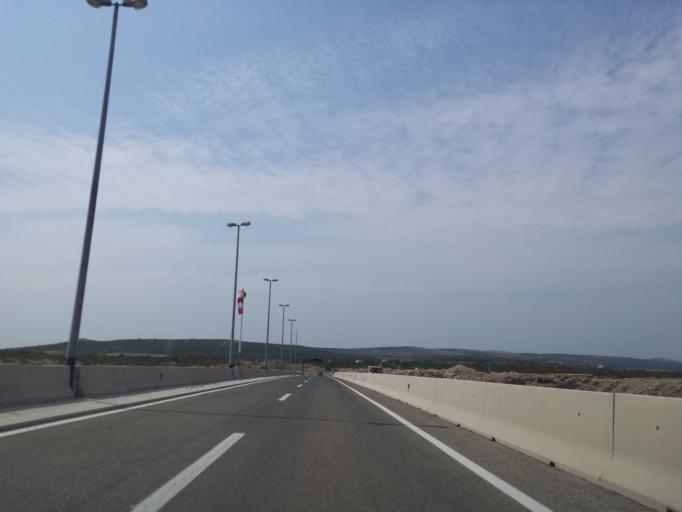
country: HR
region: Zadarska
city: Posedarje
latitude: 44.2368
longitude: 15.5223
